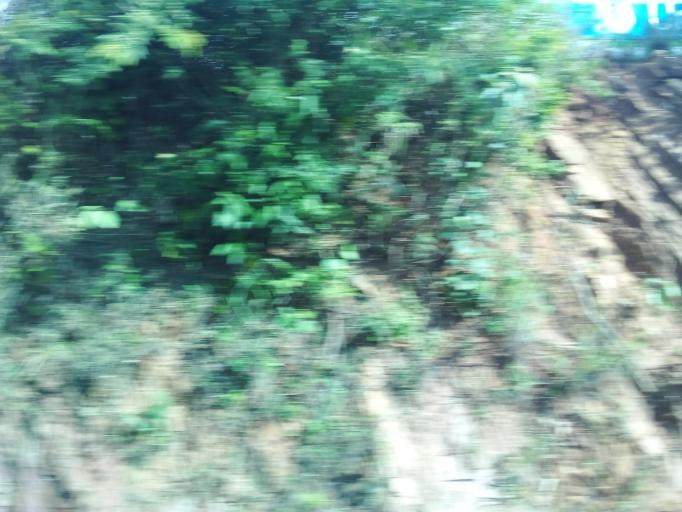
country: BR
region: Minas Gerais
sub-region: Raposos
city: Raposos
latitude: -19.8720
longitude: -43.7744
